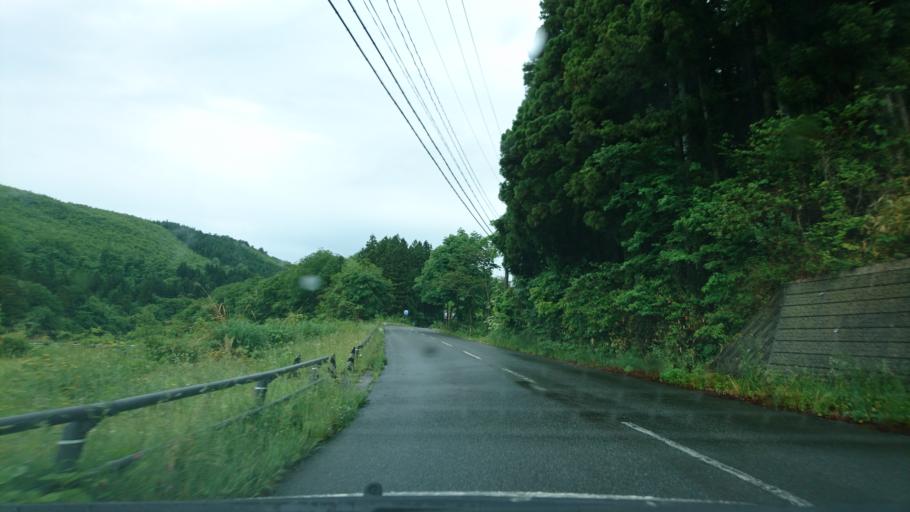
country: JP
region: Iwate
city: Ichinoseki
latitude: 38.9717
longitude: 140.9799
